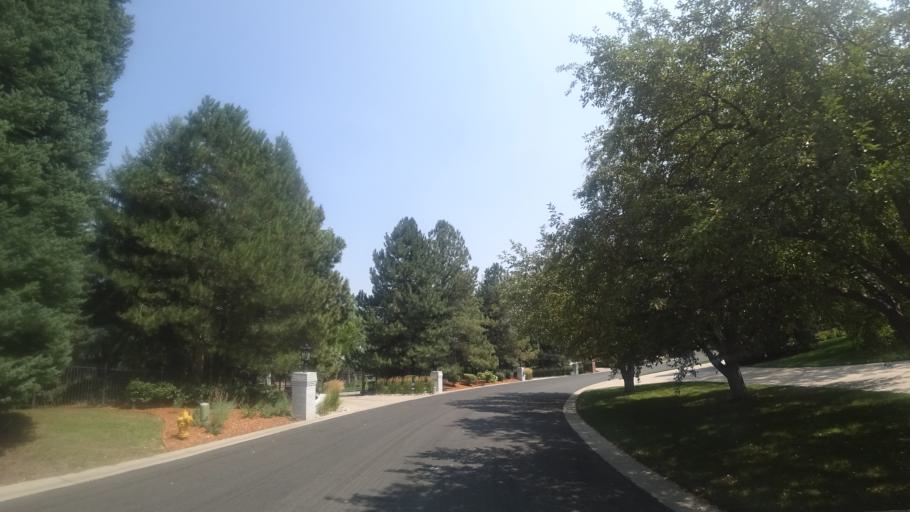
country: US
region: Colorado
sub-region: Arapahoe County
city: Cherry Hills Village
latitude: 39.6293
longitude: -104.9669
